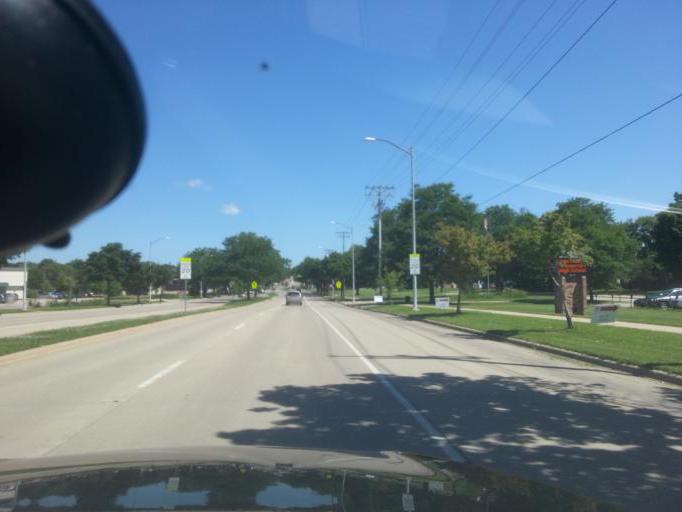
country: US
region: Wisconsin
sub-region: Dane County
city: Middleton
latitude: 43.0631
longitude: -89.5026
